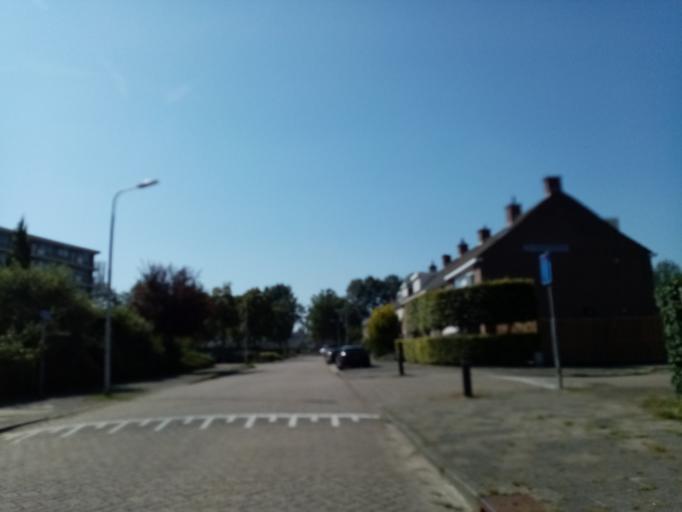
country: NL
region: South Holland
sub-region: Gemeente Lisse
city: Lisse
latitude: 52.2438
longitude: 4.5644
